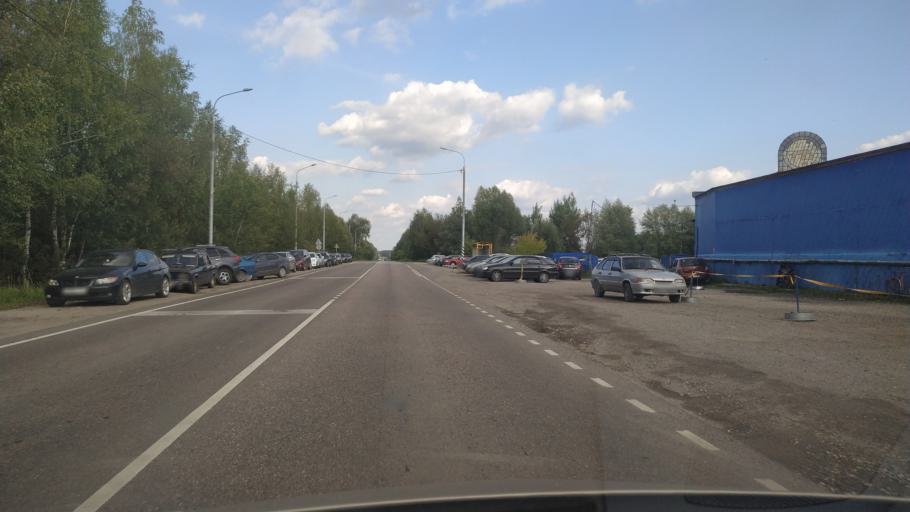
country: RU
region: Moskovskaya
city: Vereya
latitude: 55.7082
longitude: 39.1105
